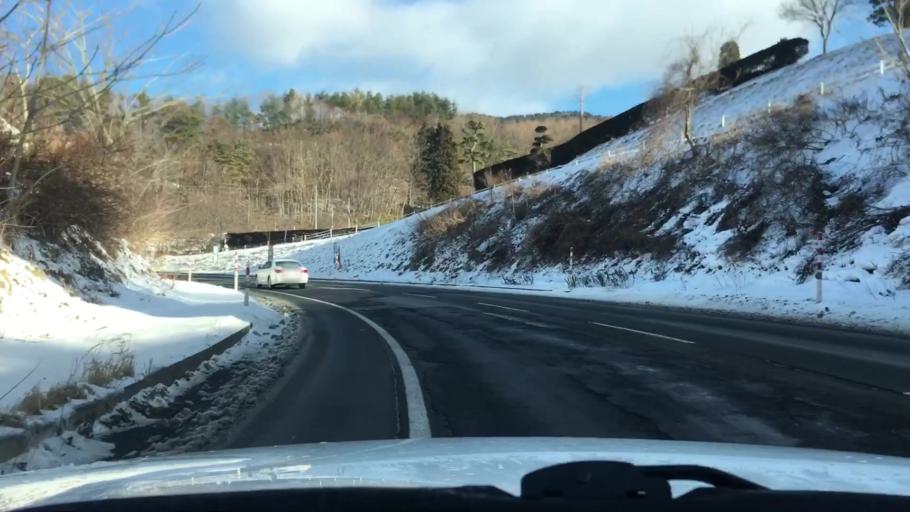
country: JP
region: Iwate
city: Morioka-shi
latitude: 39.6694
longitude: 141.3304
